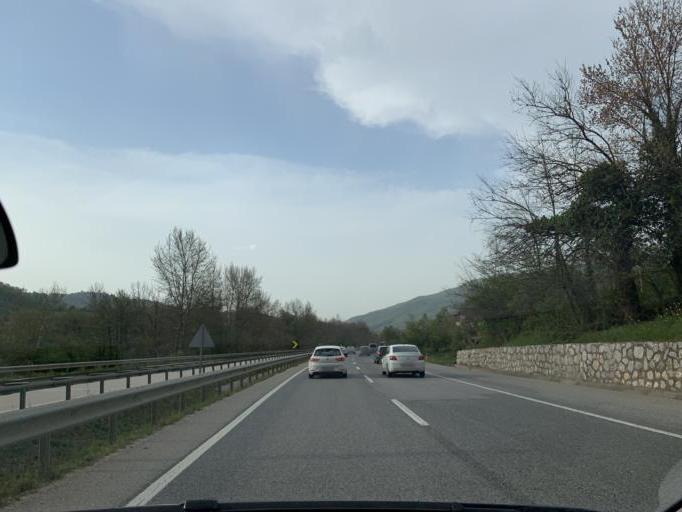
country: TR
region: Bursa
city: Tahtakopru
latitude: 39.9649
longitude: 29.6560
